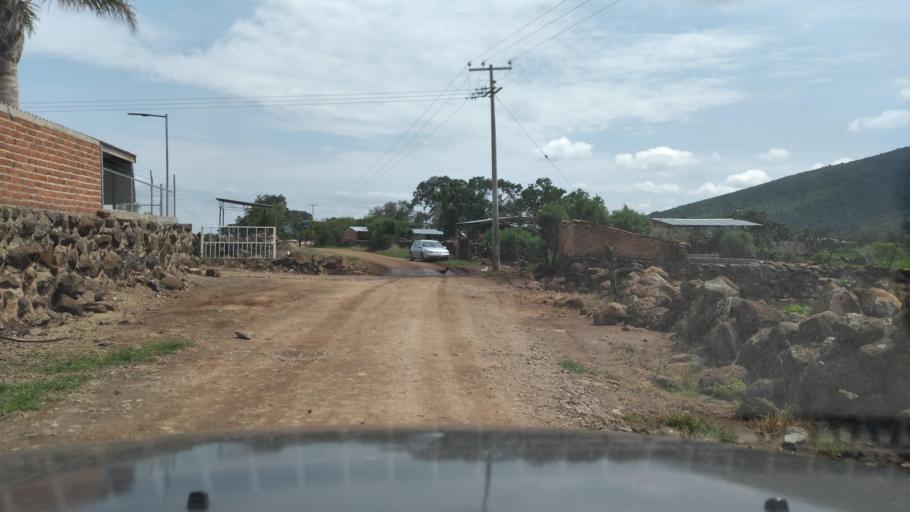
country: MX
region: Jalisco
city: Capilla de Guadalupe
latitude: 20.7448
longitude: -102.6324
